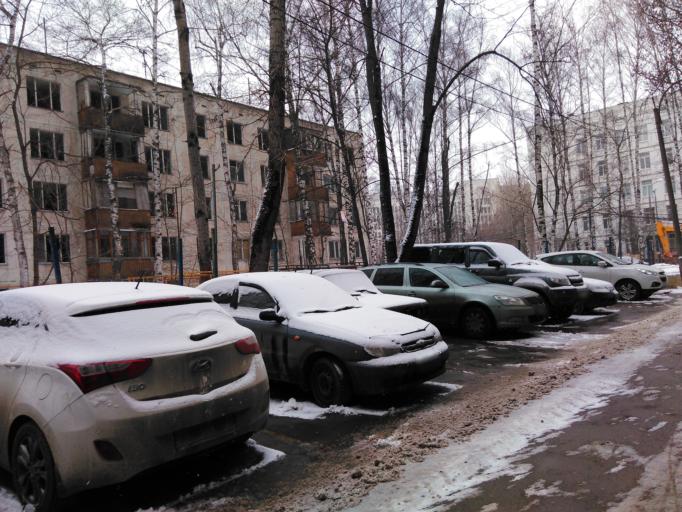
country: RU
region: Moscow
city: Nikol'skoye
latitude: 55.6713
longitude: 37.5051
